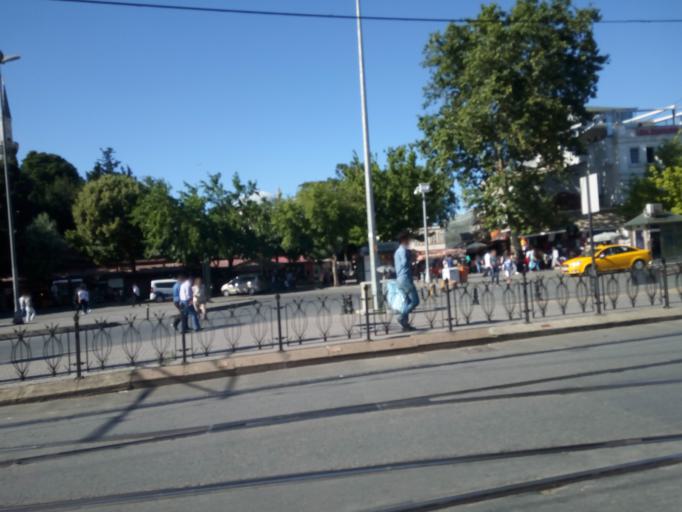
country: TR
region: Istanbul
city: Eminoenue
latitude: 41.0094
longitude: 28.9662
